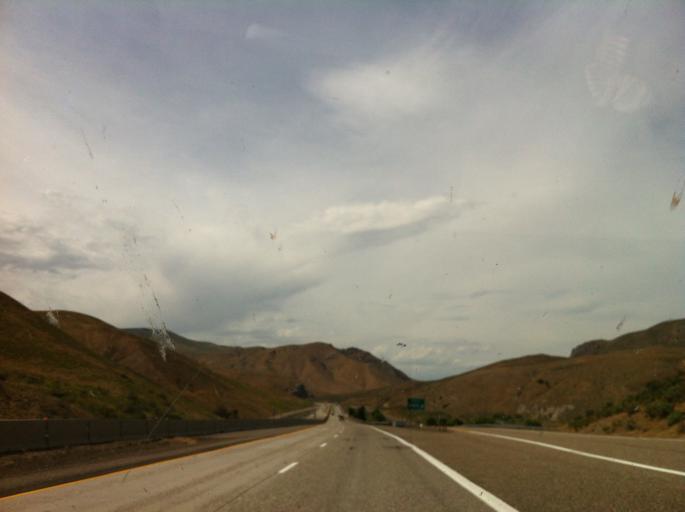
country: US
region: Idaho
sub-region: Washington County
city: Weiser
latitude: 44.3625
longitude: -117.2928
